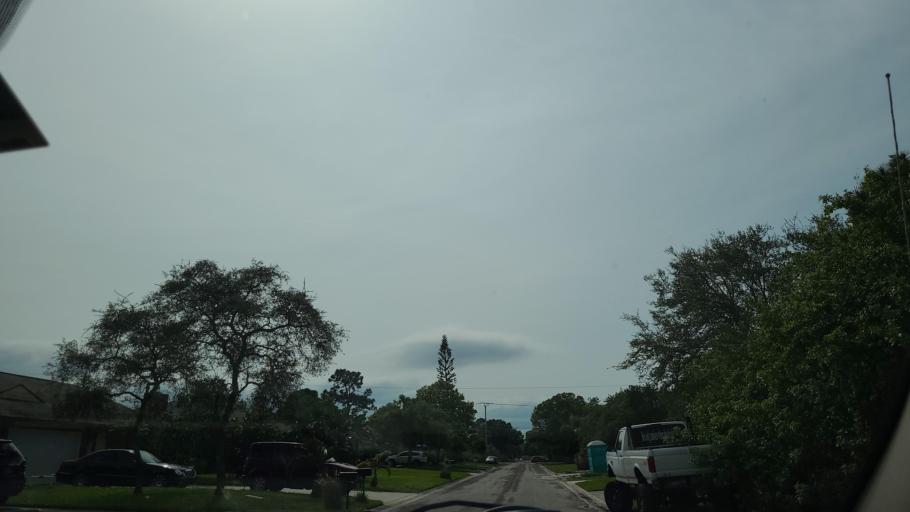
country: US
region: Florida
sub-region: Indian River County
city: Sebastian
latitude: 27.7770
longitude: -80.4642
